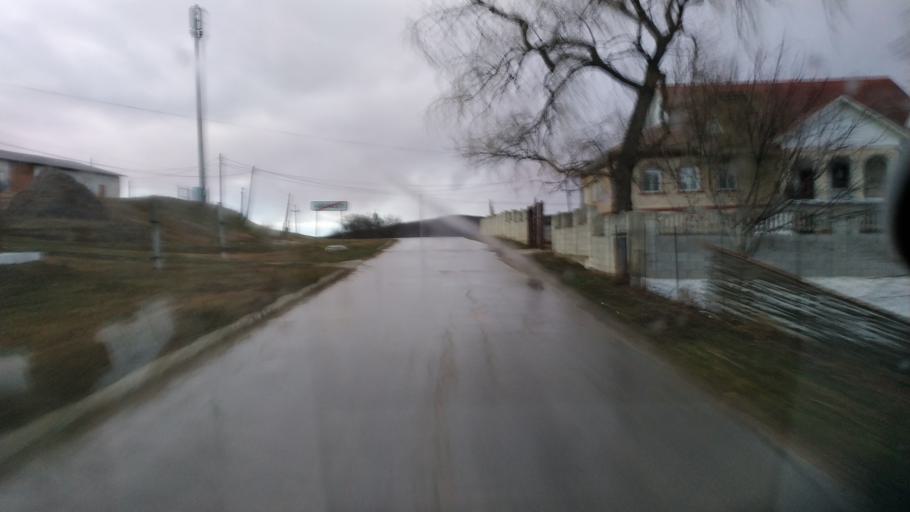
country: MD
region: Taraclia
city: Telenesti
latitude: 47.3862
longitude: 28.3247
